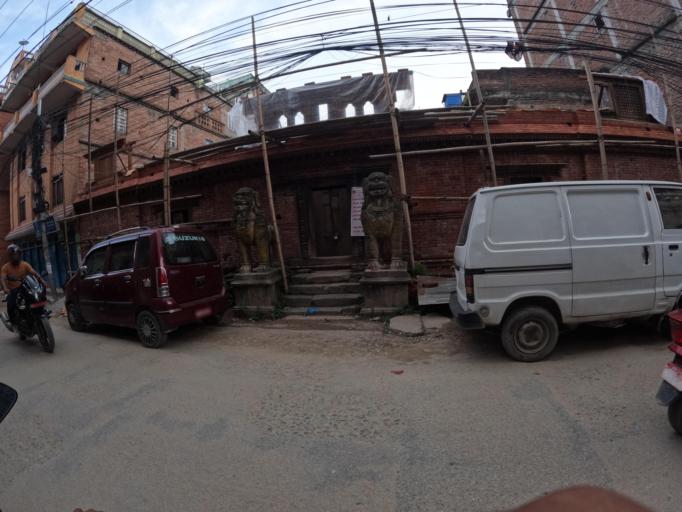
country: NP
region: Central Region
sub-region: Bagmati Zone
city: Bhaktapur
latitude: 27.6796
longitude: 85.3859
